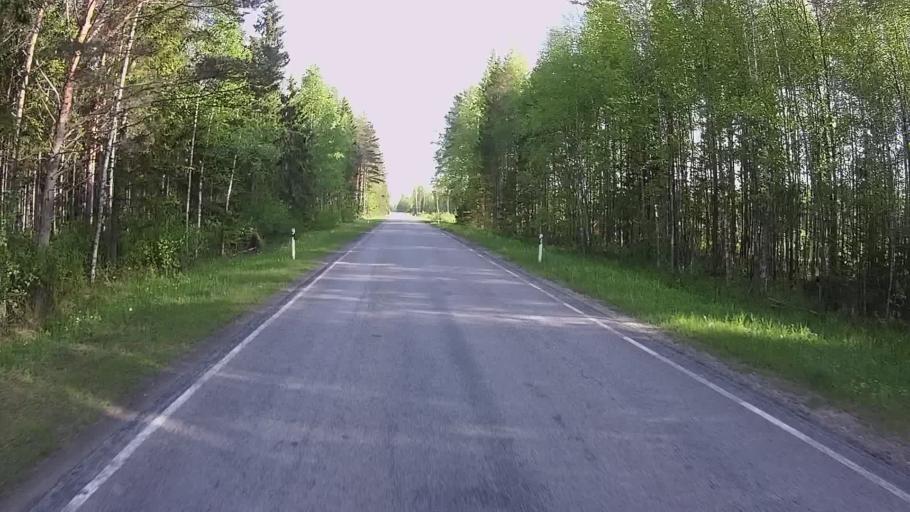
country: EE
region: Laeaene-Virumaa
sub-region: Vinni vald
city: Vinni
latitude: 59.2523
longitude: 26.6877
